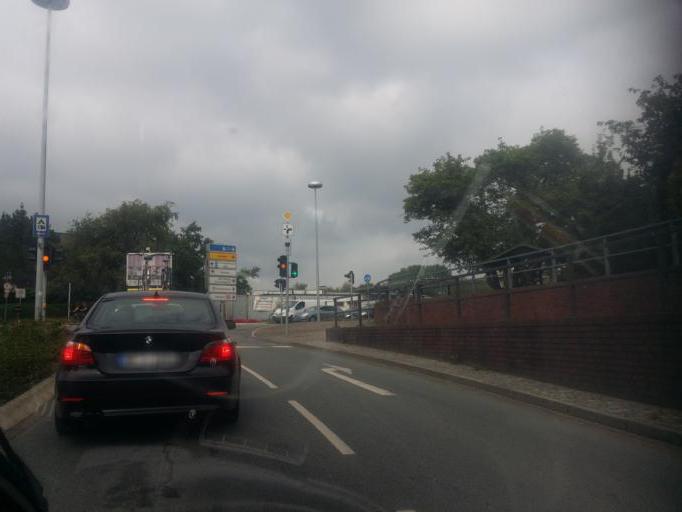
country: DE
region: Schleswig-Holstein
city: Husum
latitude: 54.4724
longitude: 9.0517
